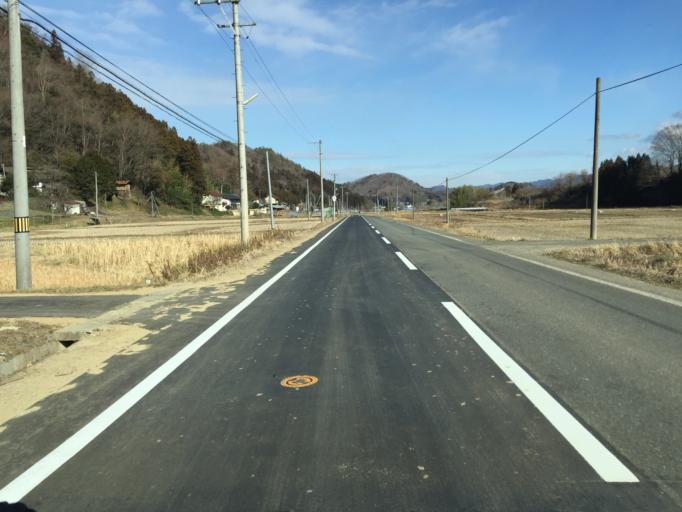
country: JP
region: Fukushima
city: Hobaramachi
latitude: 37.7527
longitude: 140.5673
